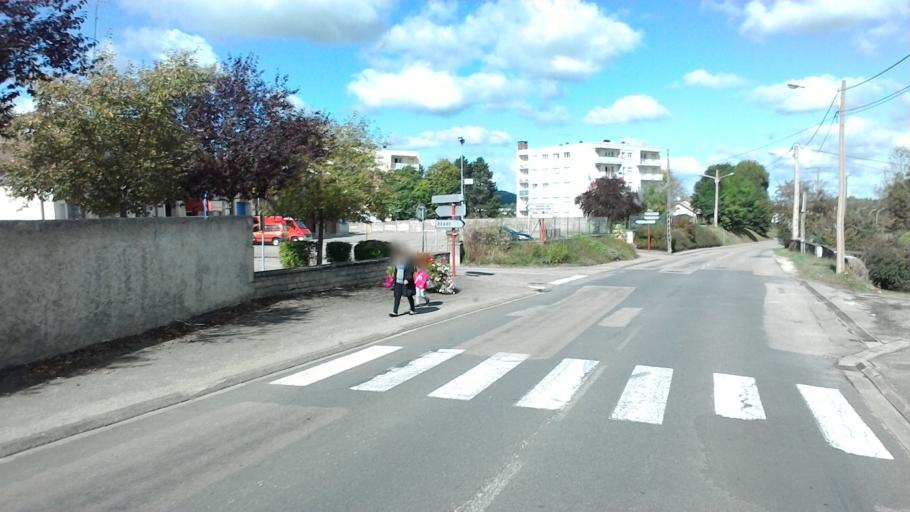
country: FR
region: Lorraine
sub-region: Departement des Vosges
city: Neufchateau
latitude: 48.3566
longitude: 5.6825
